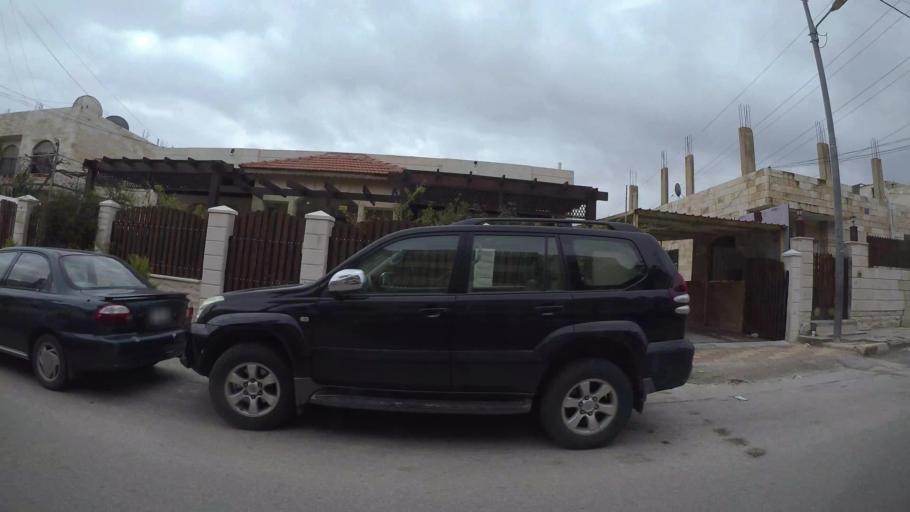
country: JO
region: Amman
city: Wadi as Sir
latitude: 31.9633
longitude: 35.8333
